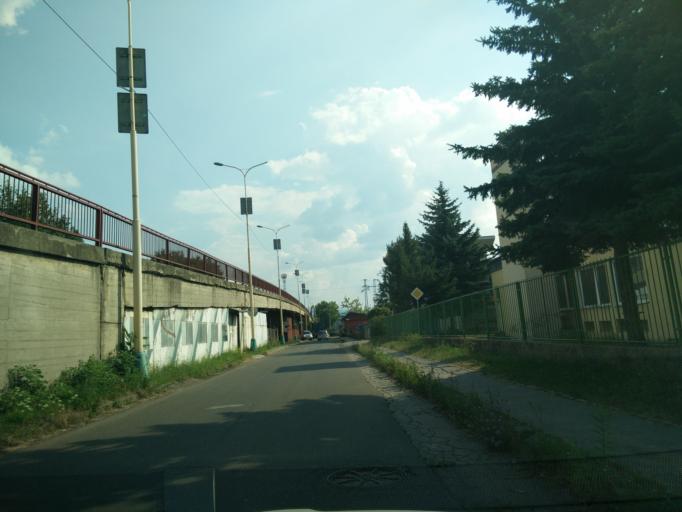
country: SK
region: Nitriansky
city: Prievidza
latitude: 48.7676
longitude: 18.6250
